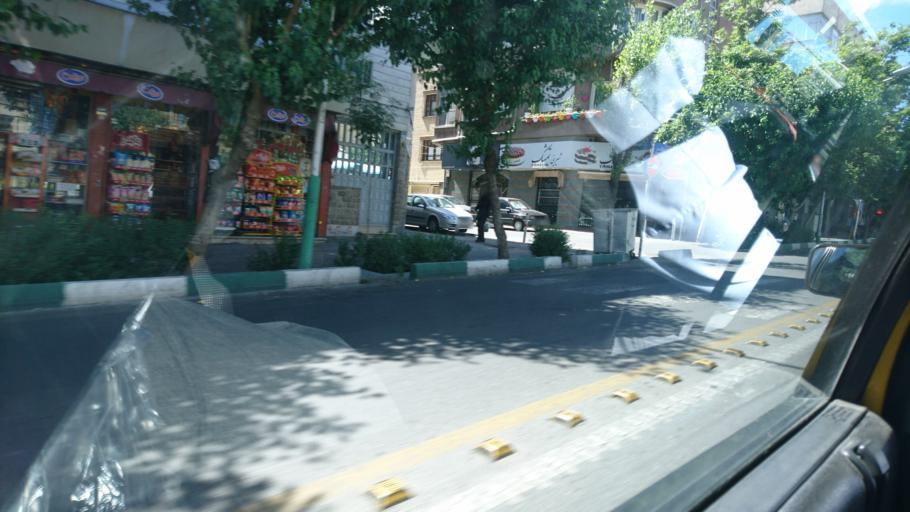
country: IR
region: Tehran
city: Tehran
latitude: 35.7012
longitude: 51.3918
